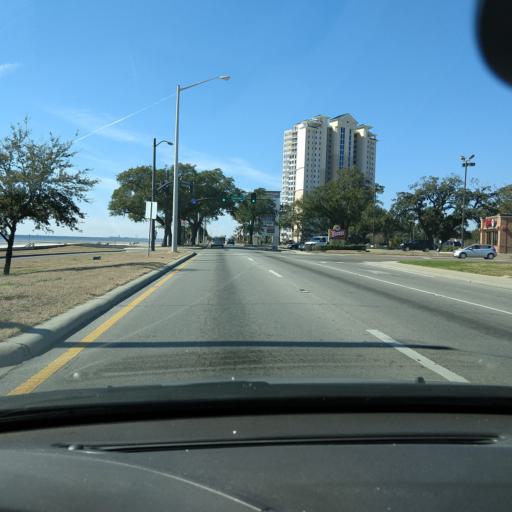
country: US
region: Mississippi
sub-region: Harrison County
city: Gulfport
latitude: 30.3891
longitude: -88.9920
